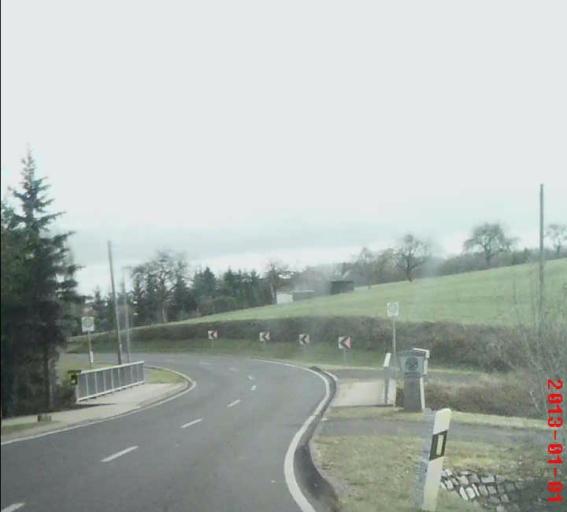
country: DE
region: Thuringia
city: Anrode
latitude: 51.2541
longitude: 10.3373
